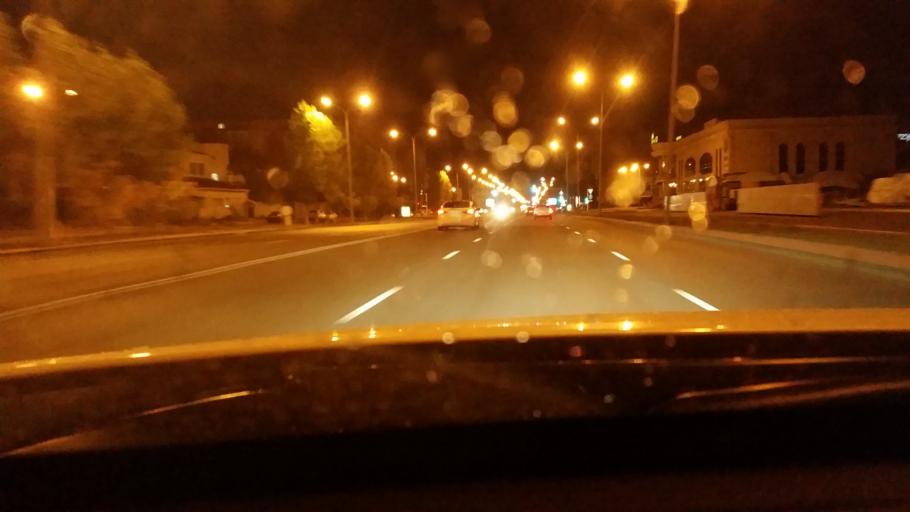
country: KZ
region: Astana Qalasy
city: Astana
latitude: 51.1460
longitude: 71.4852
